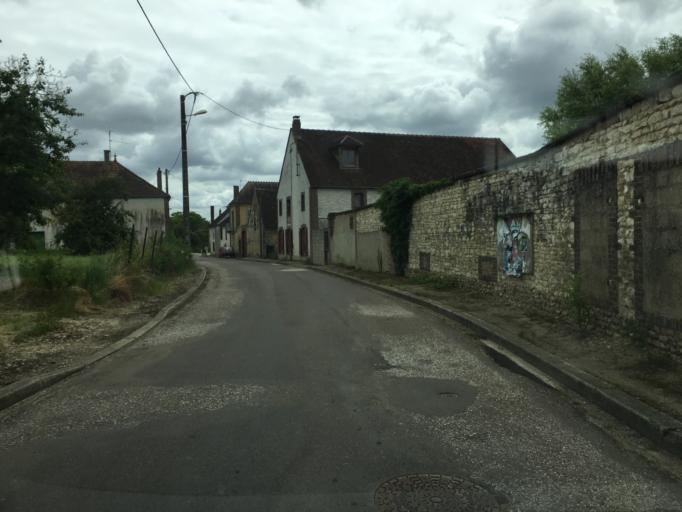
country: FR
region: Bourgogne
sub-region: Departement de l'Yonne
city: Fleury-la-Vallee
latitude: 47.8862
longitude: 3.4114
